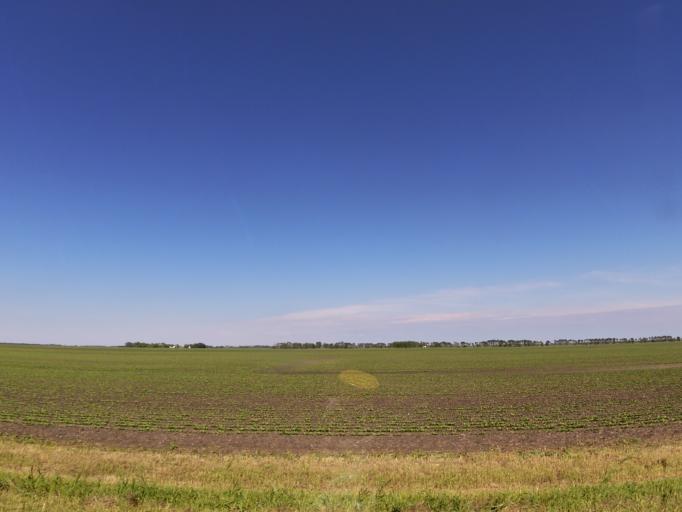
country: US
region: North Dakota
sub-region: Walsh County
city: Grafton
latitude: 48.3445
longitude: -97.2558
